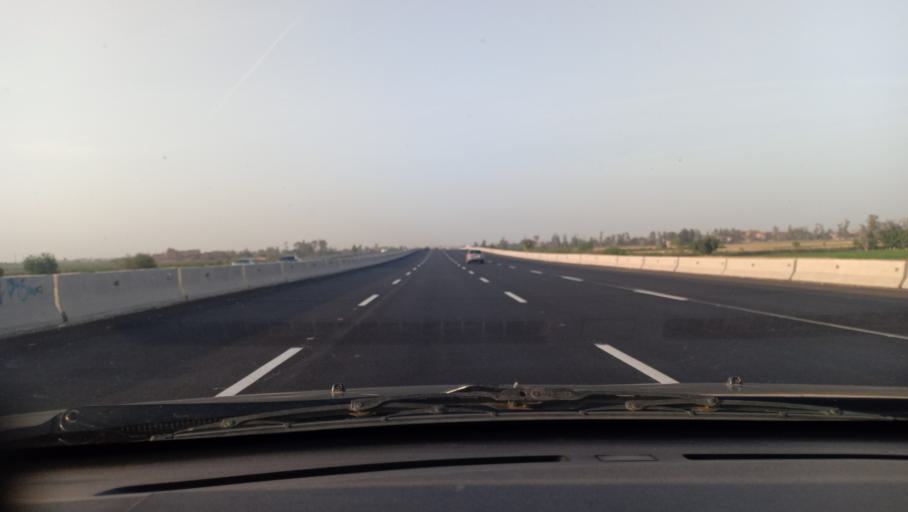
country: EG
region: Muhafazat al Qalyubiyah
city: Toukh
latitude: 30.3132
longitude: 31.2239
